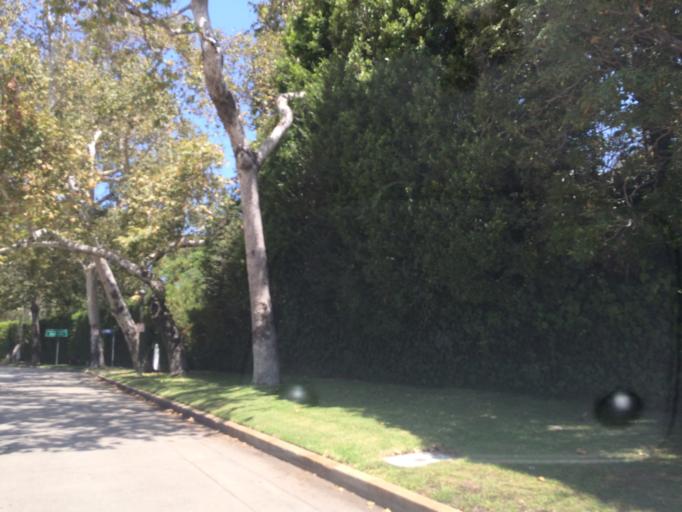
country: US
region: California
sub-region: Los Angeles County
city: Westwood, Los Angeles
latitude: 34.0796
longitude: -118.4341
